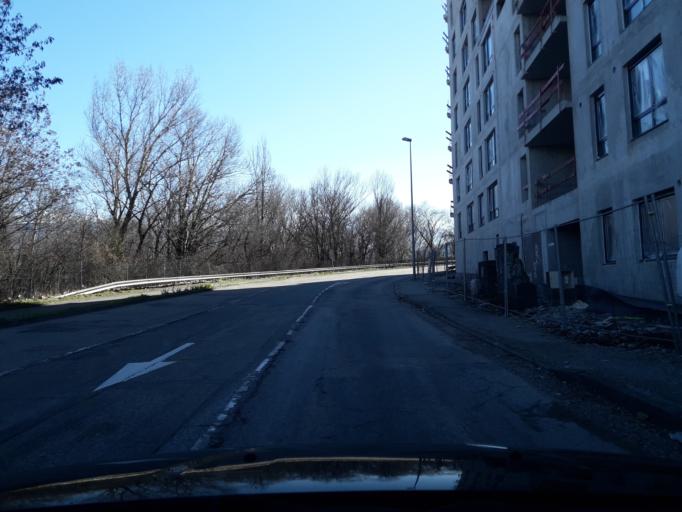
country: FR
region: Rhone-Alpes
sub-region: Departement de l'Isere
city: Echirolles
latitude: 45.1525
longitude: 5.7246
